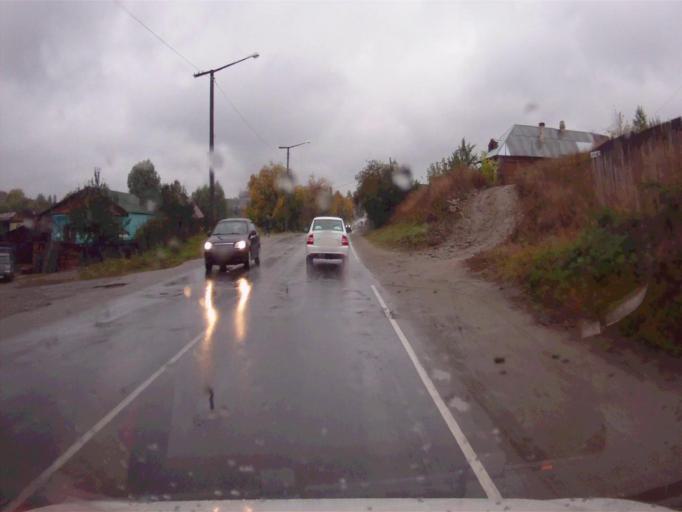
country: RU
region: Chelyabinsk
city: Kyshtym
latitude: 55.7213
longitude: 60.5370
